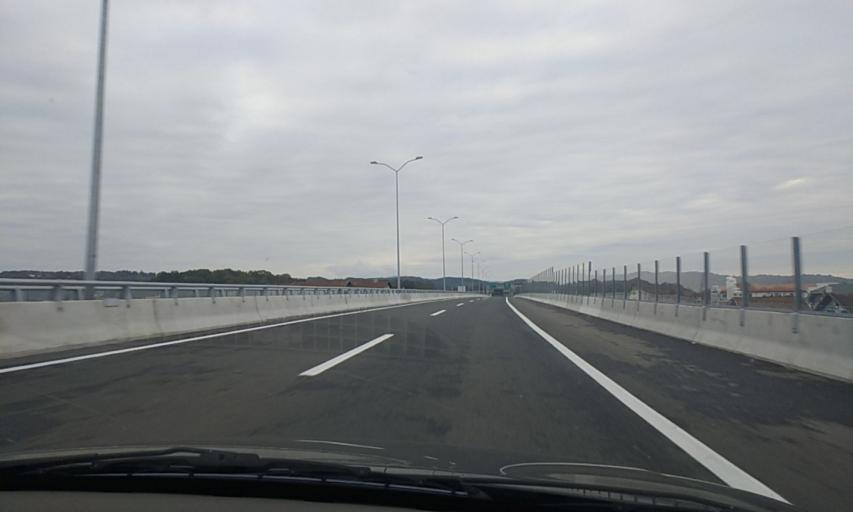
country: BA
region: Republika Srpska
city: Laktasi
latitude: 44.9183
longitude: 17.3138
